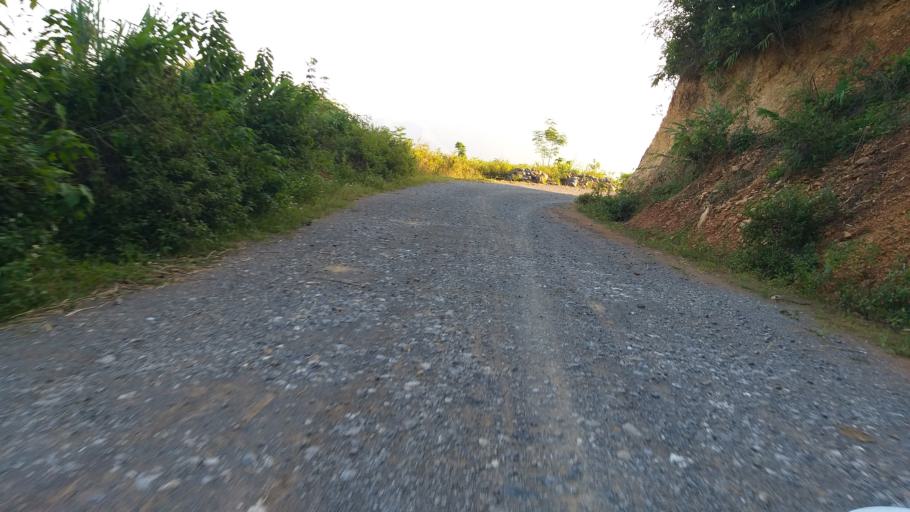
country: LA
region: Phongsali
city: Khoa
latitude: 21.1983
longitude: 102.5757
